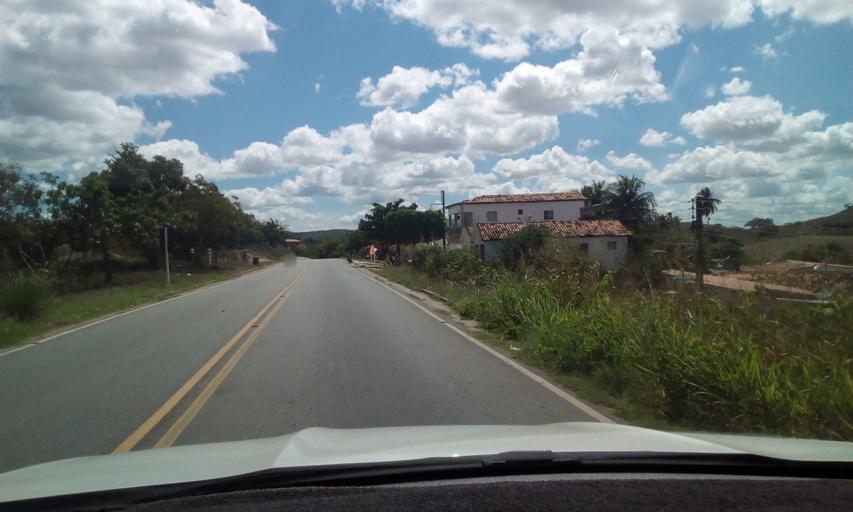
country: BR
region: Paraiba
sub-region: Serra Redonda
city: Alagoa Grande
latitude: -7.1660
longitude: -35.5920
